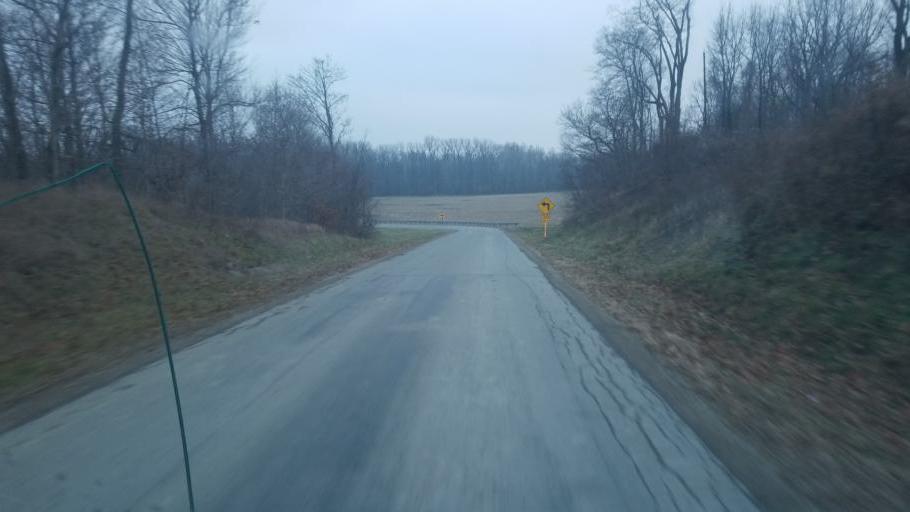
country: US
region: Ohio
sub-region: Seneca County
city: Tiffin
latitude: 40.9906
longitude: -83.2048
